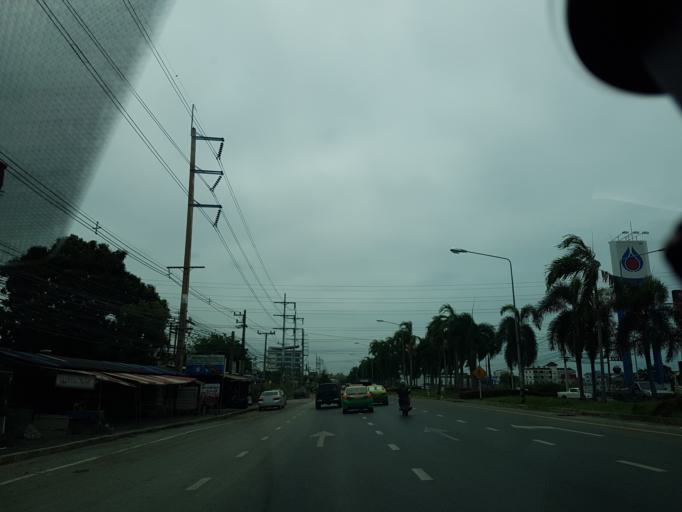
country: TH
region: Phra Nakhon Si Ayutthaya
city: Ban Bang Kadi Pathum Thani
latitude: 13.9905
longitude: 100.5824
